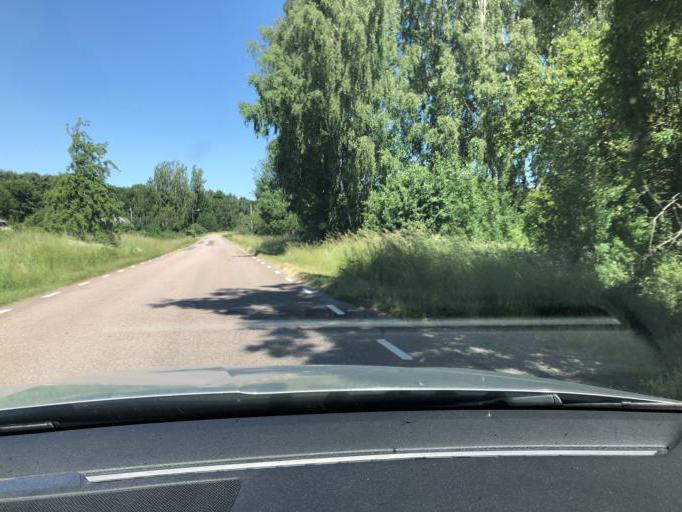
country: SE
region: Blekinge
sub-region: Olofstroms Kommun
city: Jamshog
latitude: 56.1625
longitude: 14.5985
